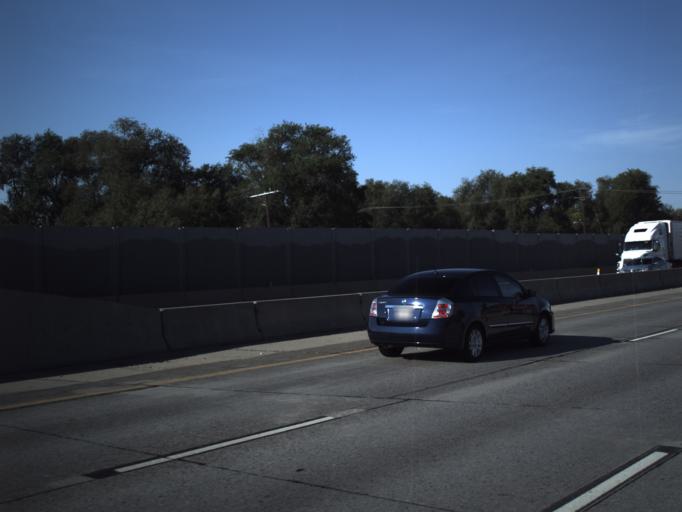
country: US
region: Utah
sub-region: Salt Lake County
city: Salt Lake City
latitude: 40.7647
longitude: -111.9239
